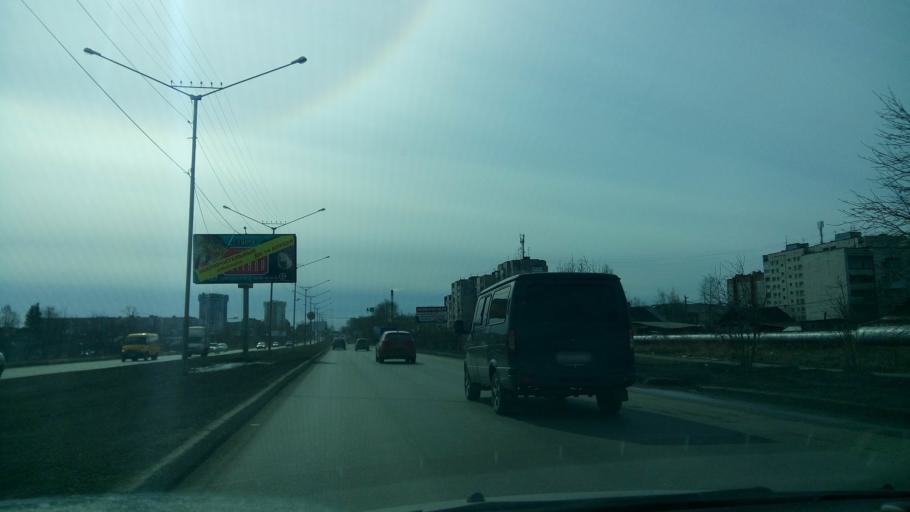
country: RU
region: Sverdlovsk
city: Nizhniy Tagil
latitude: 57.8914
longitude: 59.9408
